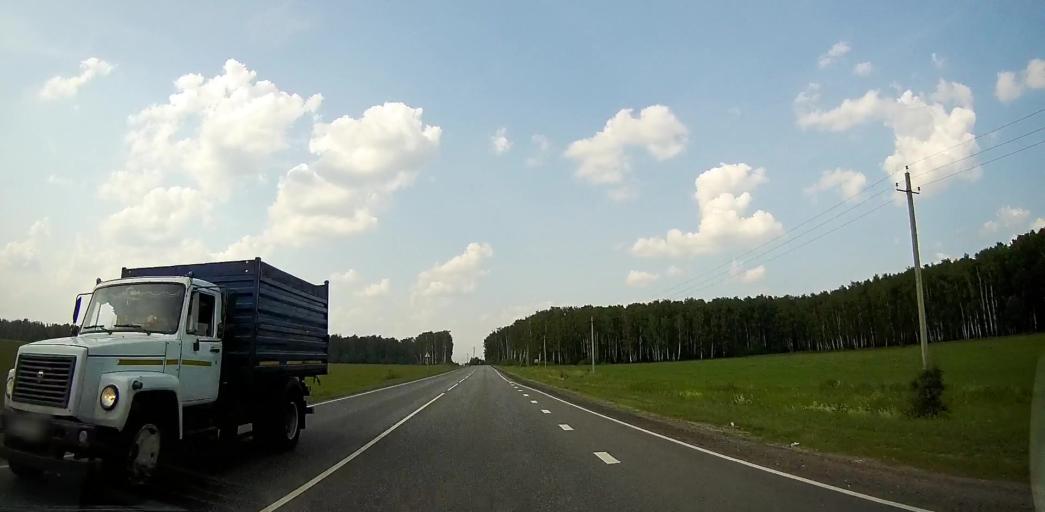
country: RU
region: Moskovskaya
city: Malino
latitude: 55.0502
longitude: 38.1461
